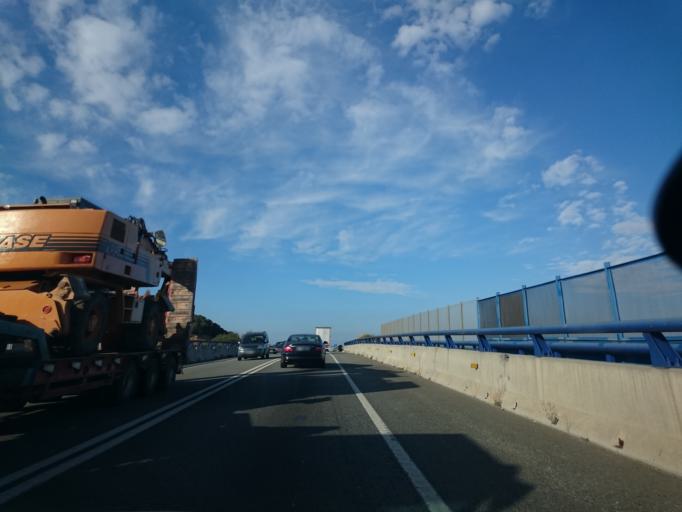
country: ES
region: Catalonia
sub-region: Provincia de Barcelona
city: Castellet
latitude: 41.2988
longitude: 1.6329
